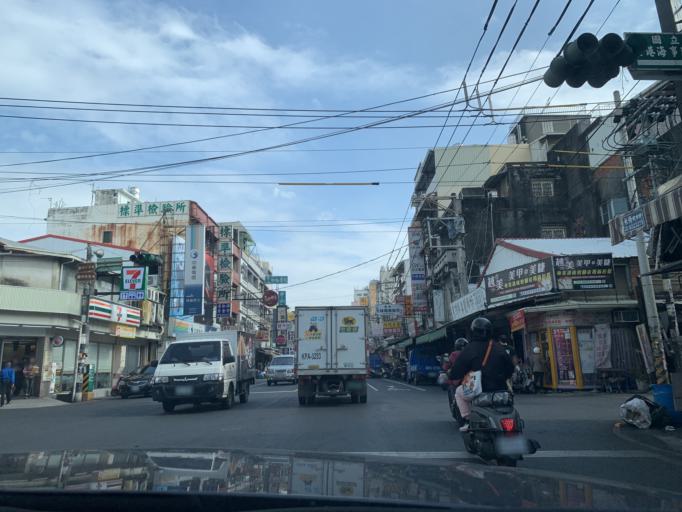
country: TW
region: Taiwan
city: Fengshan
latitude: 22.4677
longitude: 120.4483
